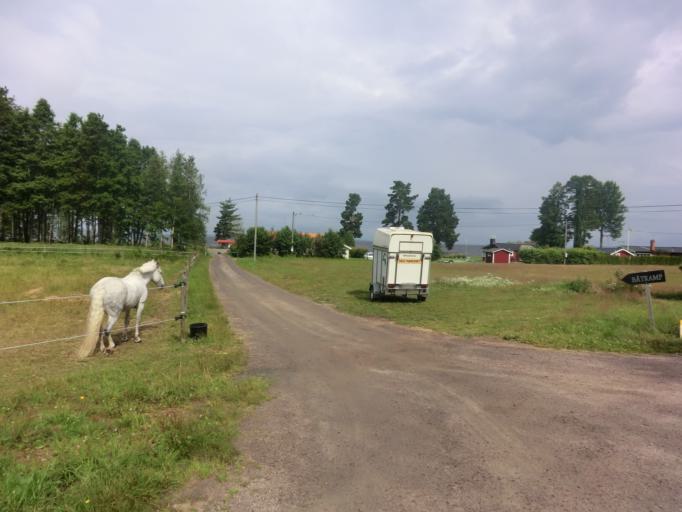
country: SE
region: Vaestra Goetaland
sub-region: Gullspangs Kommun
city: Anderstorp
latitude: 58.9107
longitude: 14.2926
